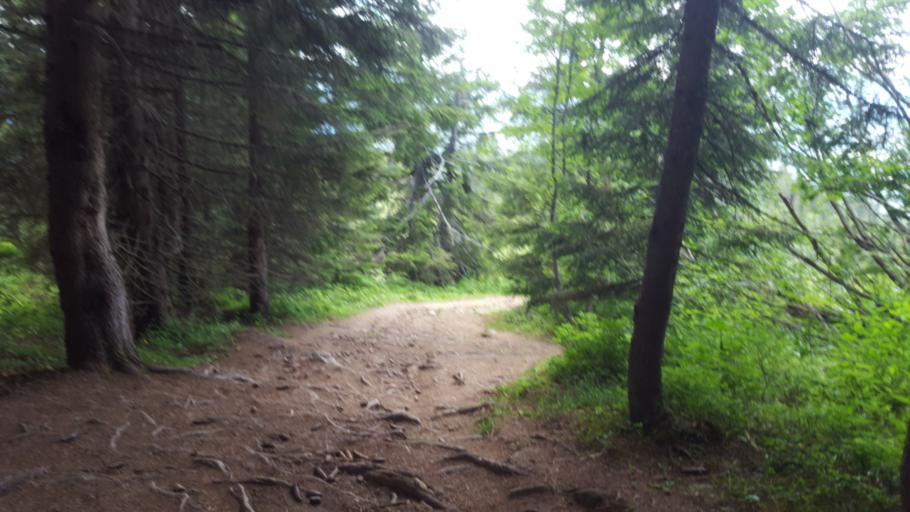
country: FR
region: Rhone-Alpes
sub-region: Departement de la Haute-Savoie
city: Le Grand-Bornand
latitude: 45.9217
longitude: 6.4439
